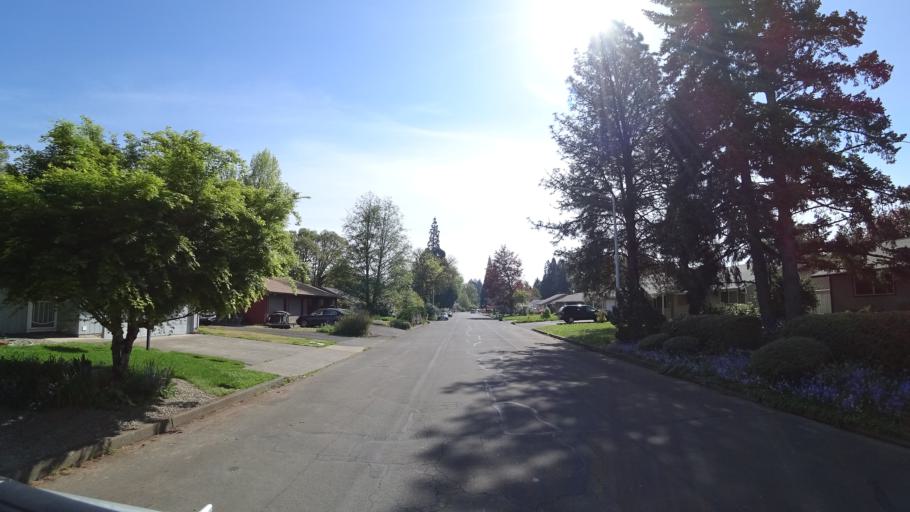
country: US
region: Oregon
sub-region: Washington County
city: Hillsboro
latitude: 45.5233
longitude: -122.9436
